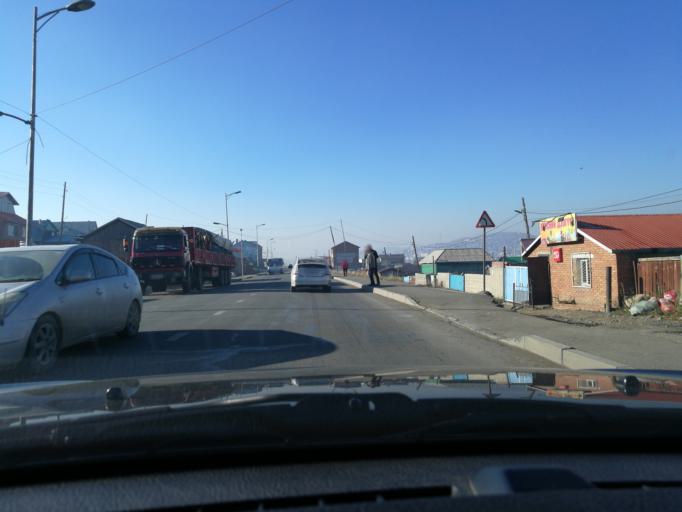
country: MN
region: Ulaanbaatar
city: Ulaanbaatar
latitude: 47.9750
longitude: 106.9328
